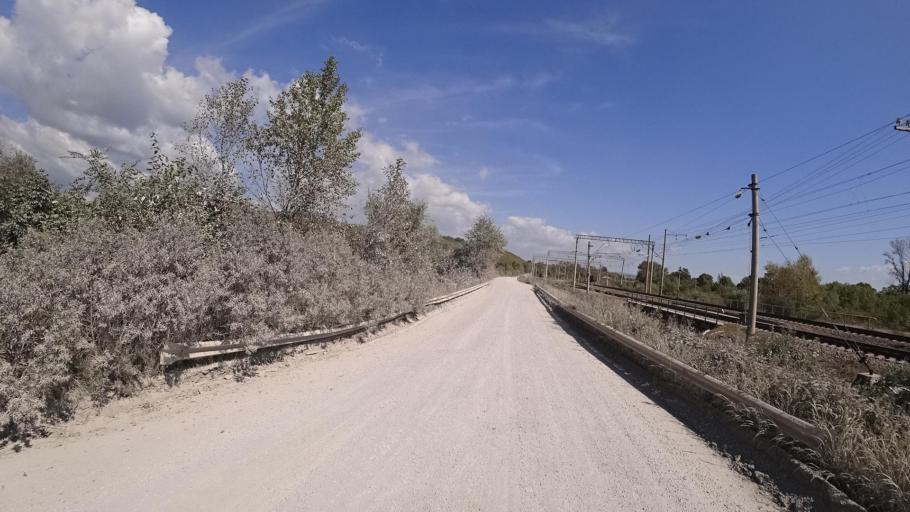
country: RU
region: Jewish Autonomous Oblast
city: Londoko
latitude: 49.0065
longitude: 131.9366
